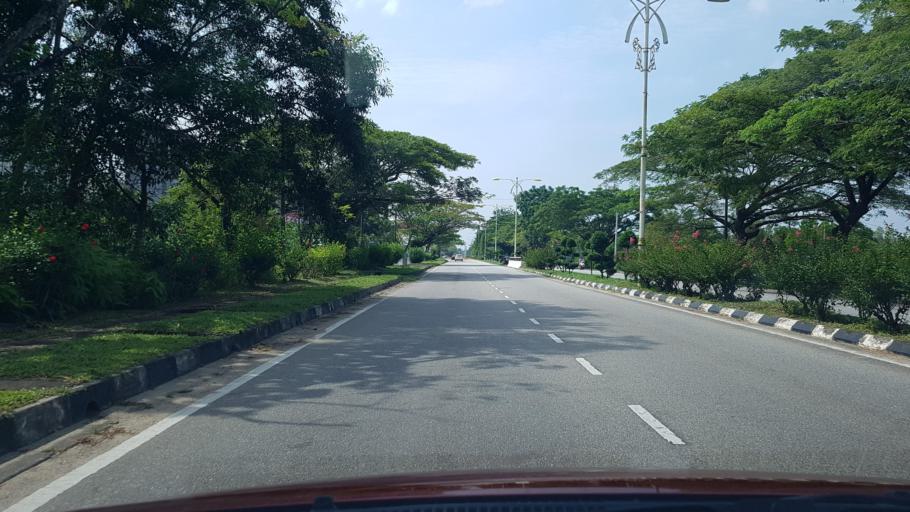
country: MY
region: Terengganu
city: Kuala Terengganu
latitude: 5.3465
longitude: 103.1025
